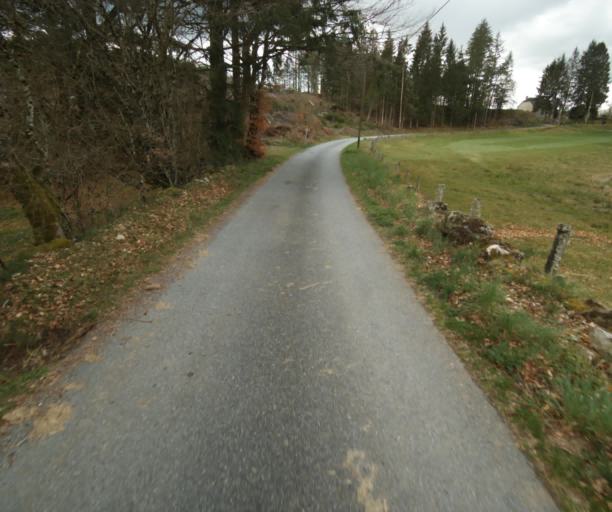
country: FR
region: Limousin
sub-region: Departement de la Correze
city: Correze
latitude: 45.2692
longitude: 1.9593
